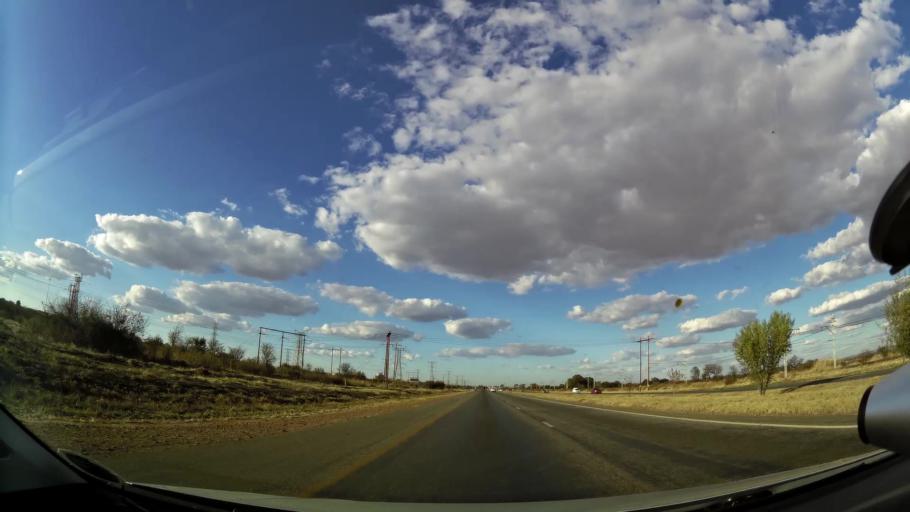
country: ZA
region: North-West
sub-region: Dr Kenneth Kaunda District Municipality
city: Potchefstroom
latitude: -26.7331
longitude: 27.0577
